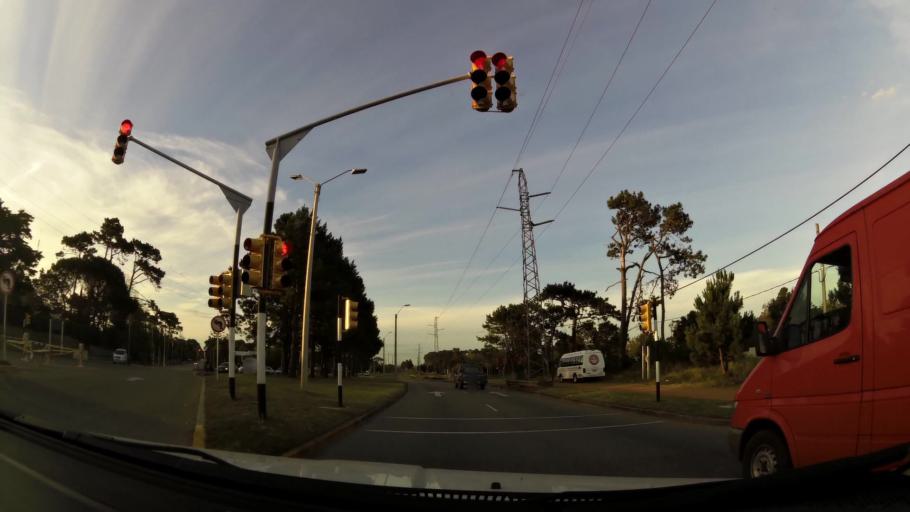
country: UY
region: Maldonado
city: Maldonado
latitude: -34.9256
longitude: -54.9412
